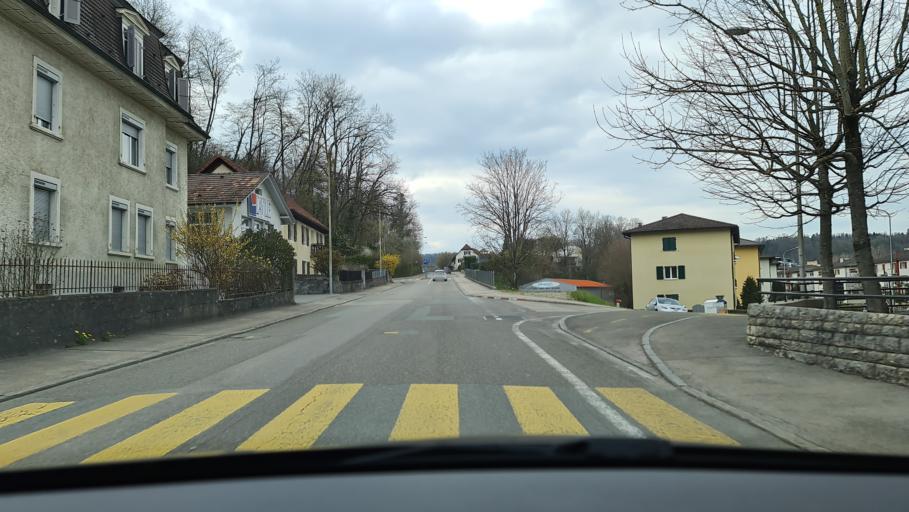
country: CH
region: Jura
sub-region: Porrentruy District
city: Porrentruy
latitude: 47.4224
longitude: 7.0772
